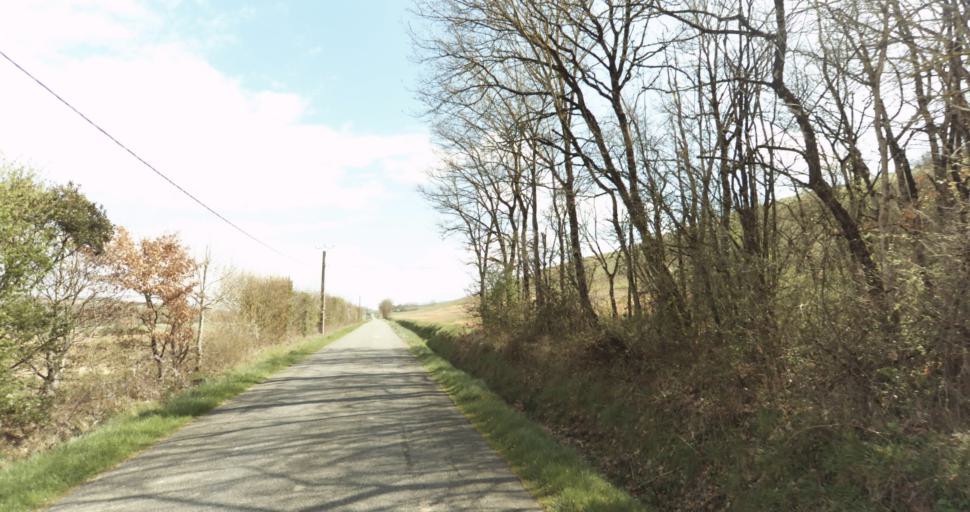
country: FR
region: Midi-Pyrenees
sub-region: Departement de la Haute-Garonne
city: Auterive
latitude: 43.3707
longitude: 1.5160
